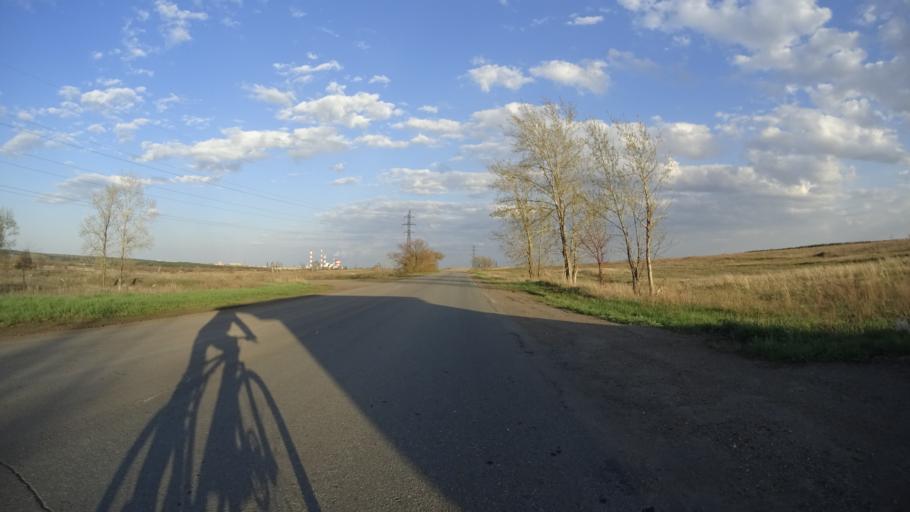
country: RU
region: Chelyabinsk
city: Troitsk
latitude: 54.0538
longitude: 61.5898
